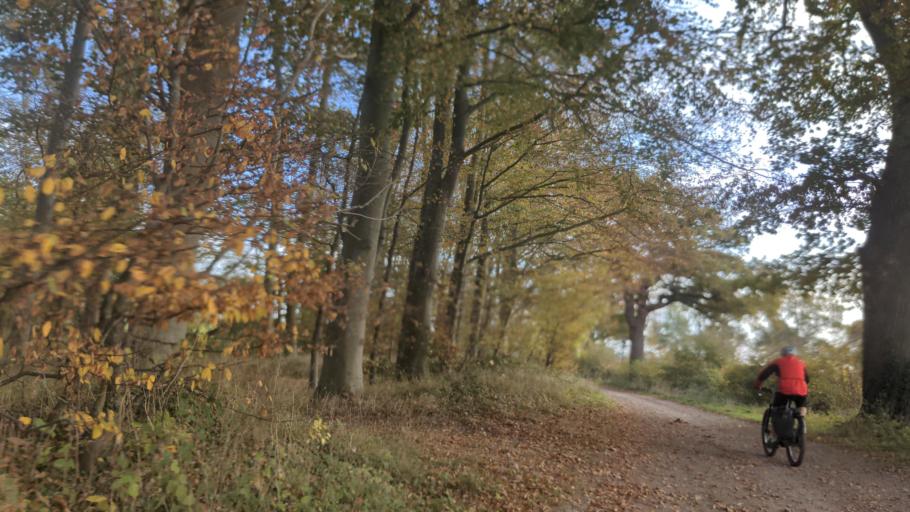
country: DE
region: Schleswig-Holstein
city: Neustadt in Holstein
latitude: 54.1244
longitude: 10.7871
